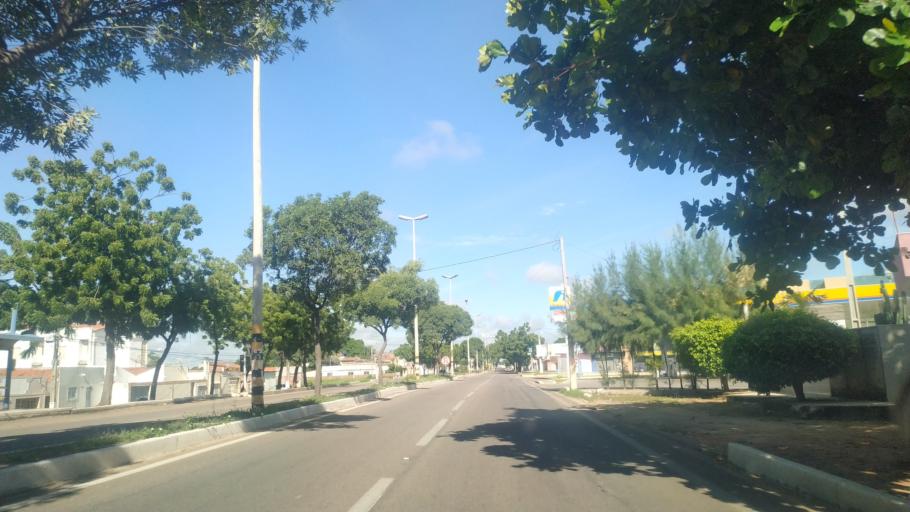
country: BR
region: Rio Grande do Norte
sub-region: Mossoro
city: Mossoro
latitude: -5.1921
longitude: -37.3661
